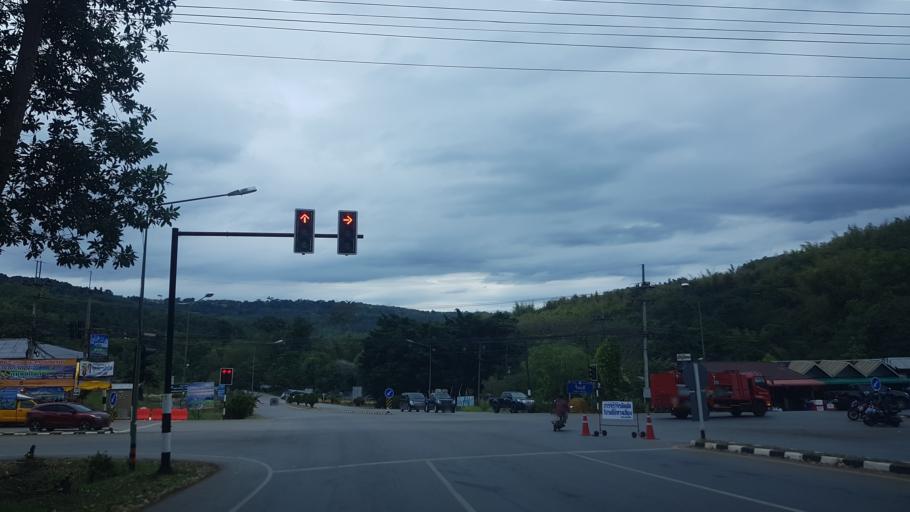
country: TH
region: Phetchabun
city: Khao Kho
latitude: 16.5712
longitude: 100.9893
